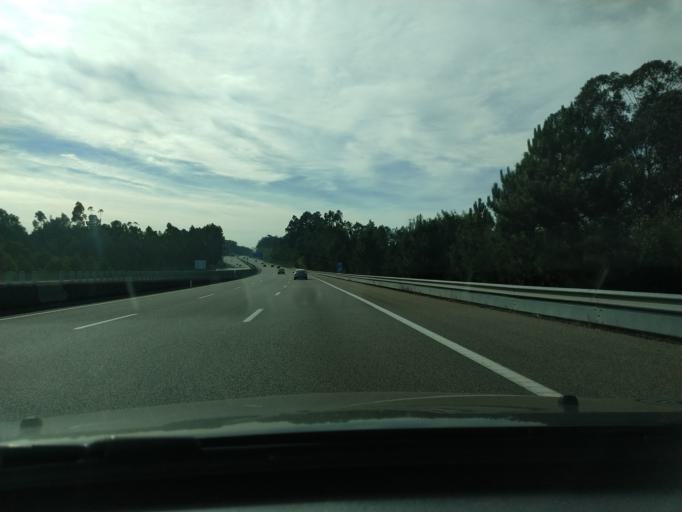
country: PT
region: Aveiro
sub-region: Santa Maria da Feira
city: Rio Meao
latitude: 40.9384
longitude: -8.5738
